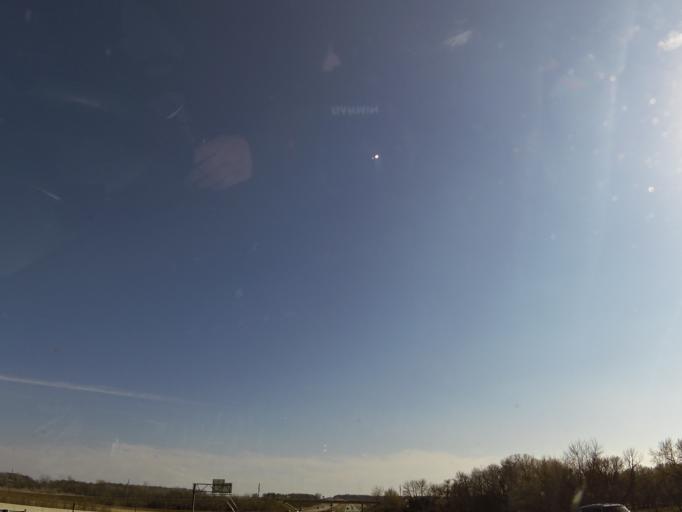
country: US
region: Minnesota
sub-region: Steele County
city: Owatonna
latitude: 44.0549
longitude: -93.2500
